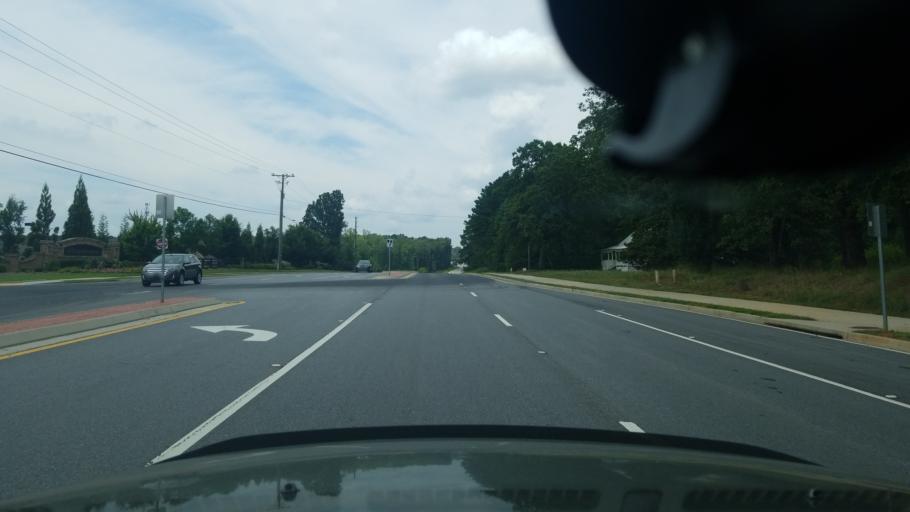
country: US
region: Georgia
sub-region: Fulton County
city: Milton
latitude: 34.1509
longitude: -84.2329
